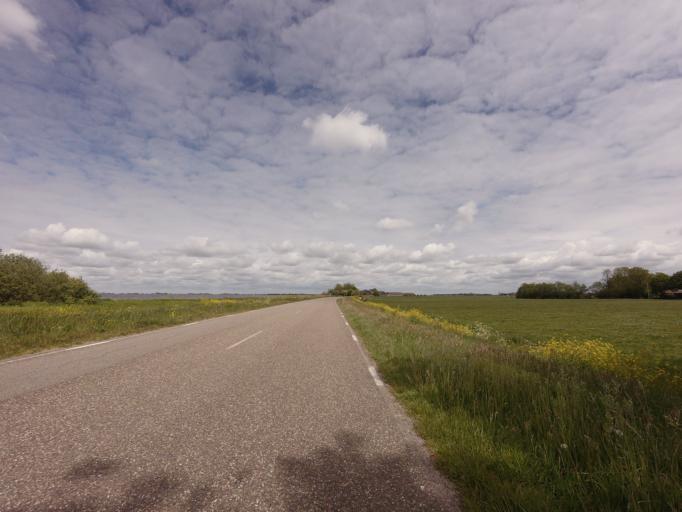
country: NL
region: Friesland
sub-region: Gemeente Gaasterlan-Sleat
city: Balk
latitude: 52.9333
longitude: 5.5511
